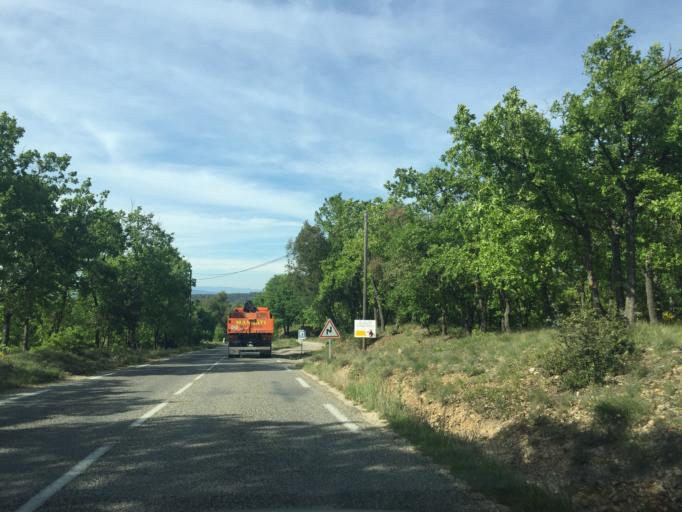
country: FR
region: Provence-Alpes-Cote d'Azur
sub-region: Departement du Var
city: Vinon-sur-Verdon
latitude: 43.7130
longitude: 5.8150
